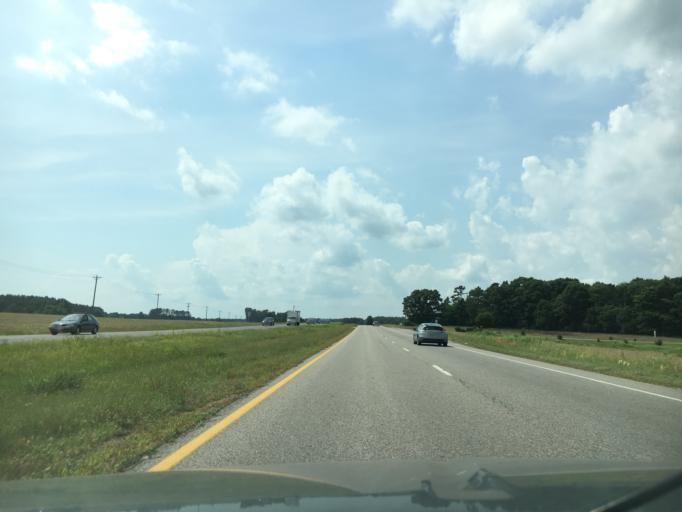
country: US
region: Virginia
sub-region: Amelia County
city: Amelia Court House
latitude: 37.3616
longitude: -77.8925
